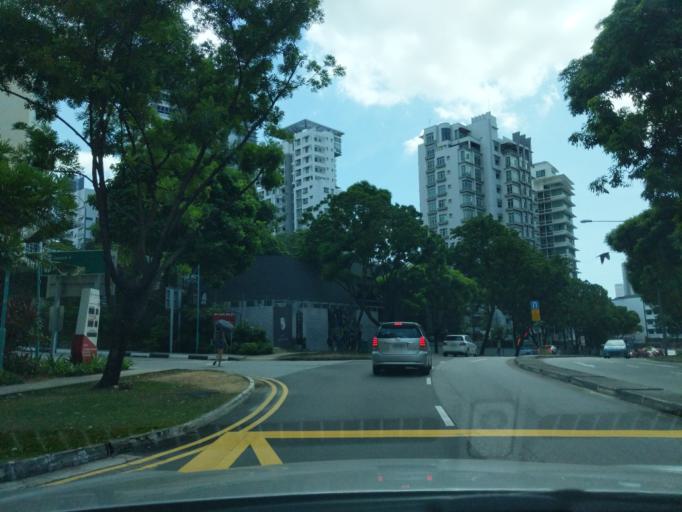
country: SG
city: Singapore
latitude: 1.3202
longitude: 103.8455
